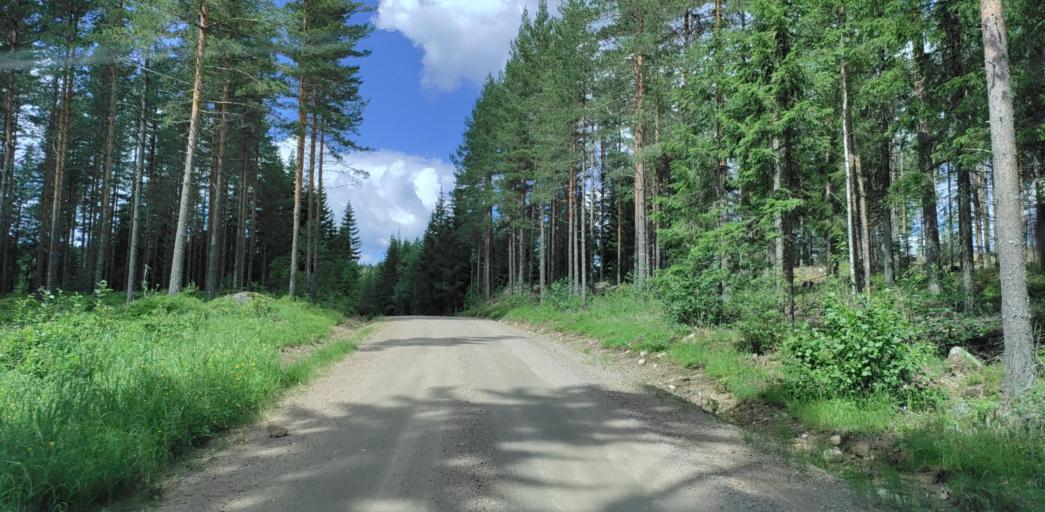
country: SE
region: Vaermland
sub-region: Hagfors Kommun
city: Ekshaerad
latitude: 60.1002
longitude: 13.3911
